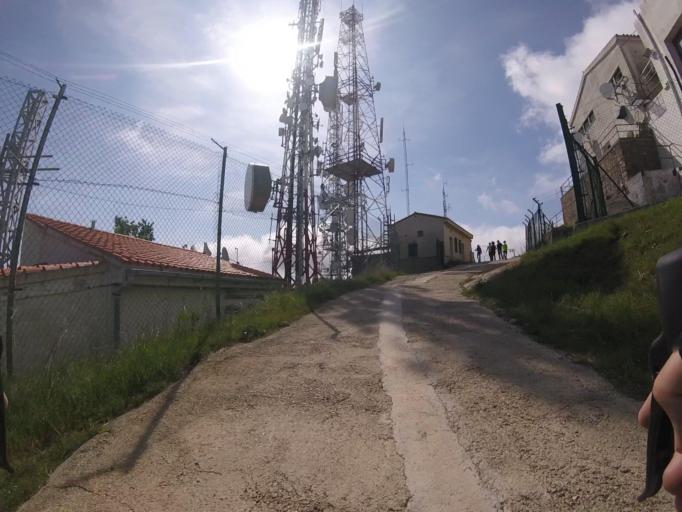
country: ES
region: Valencia
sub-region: Provincia de Castello
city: Benicassim
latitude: 40.0857
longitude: 0.0314
